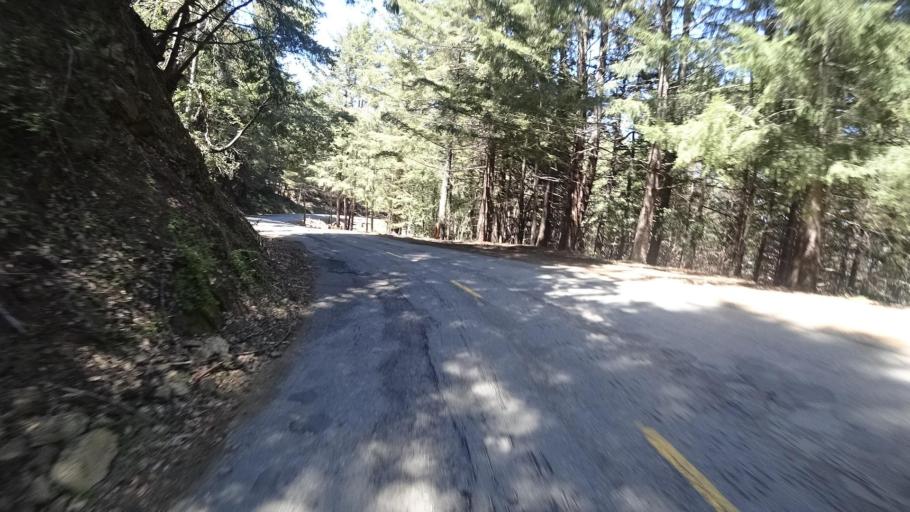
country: US
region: California
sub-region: Humboldt County
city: Rio Dell
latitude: 40.2939
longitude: -124.0568
